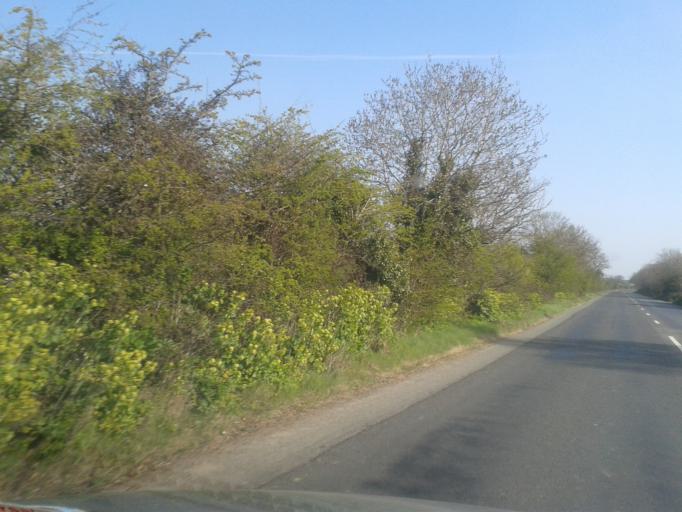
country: IE
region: Leinster
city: Balrothery
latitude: 53.5779
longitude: -6.2011
